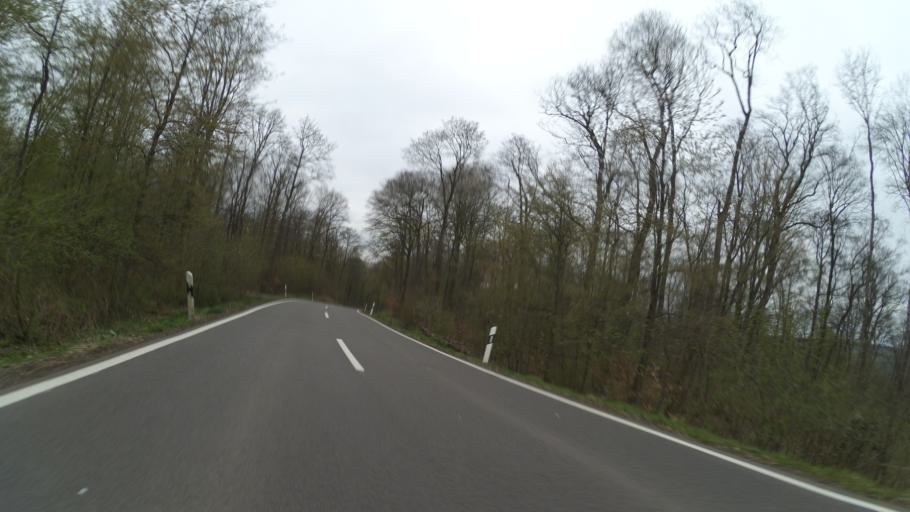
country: DE
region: Saarland
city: Friedrichsthal
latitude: 49.3011
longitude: 7.0888
